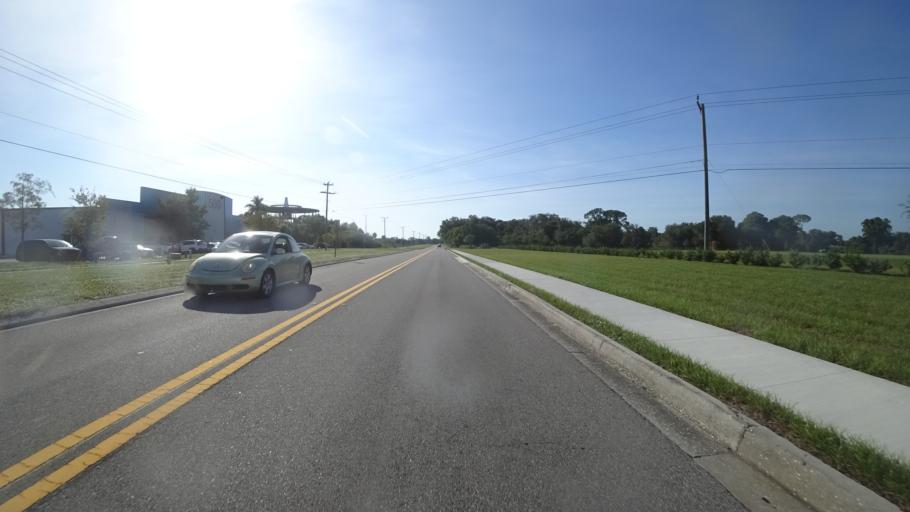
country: US
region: Florida
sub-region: Manatee County
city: Whitfield
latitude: 27.4077
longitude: -82.5620
